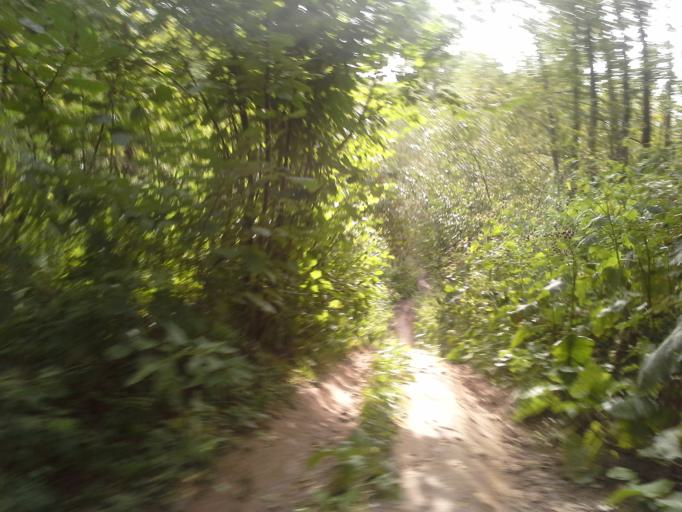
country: RU
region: Moskovskaya
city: Poselok Mar'ino
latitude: 55.5248
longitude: 37.3242
